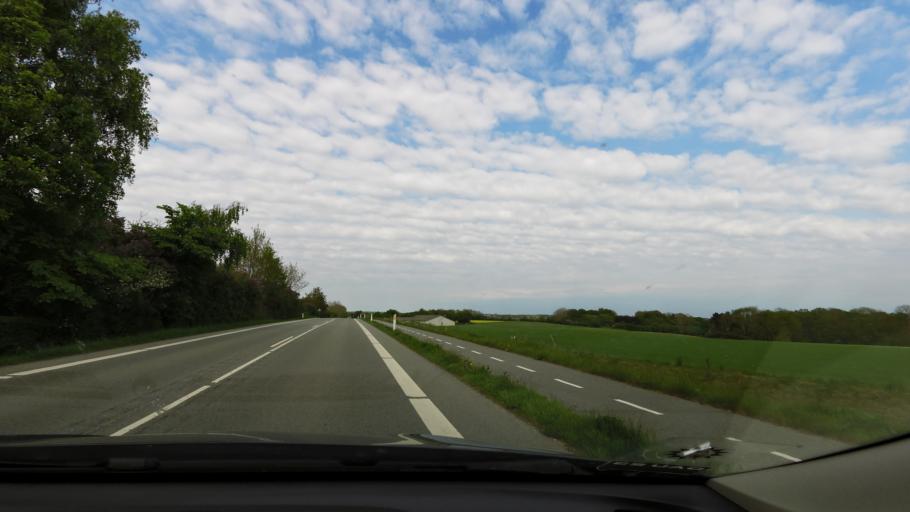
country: DK
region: South Denmark
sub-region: Nyborg Kommune
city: Nyborg
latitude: 55.2960
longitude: 10.7122
